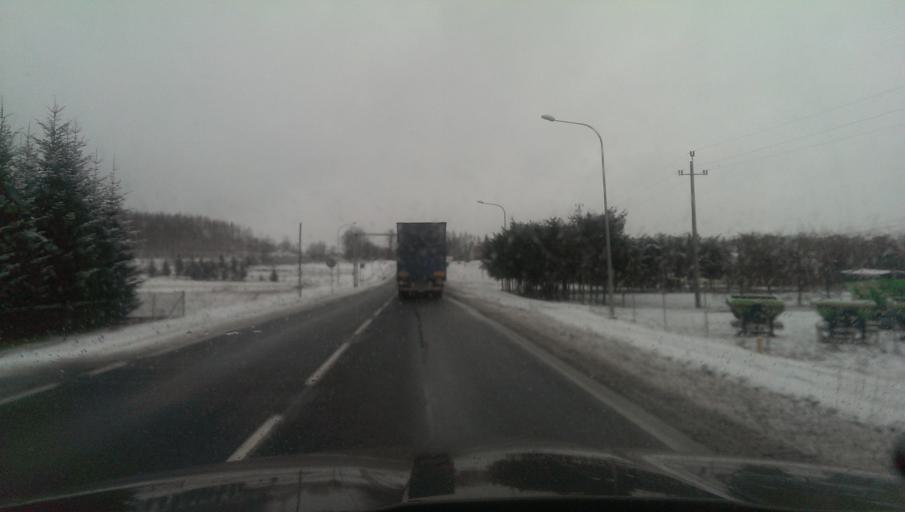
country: PL
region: Subcarpathian Voivodeship
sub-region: Powiat sanocki
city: Nowosielce-Gniewosz
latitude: 49.5741
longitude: 22.0573
